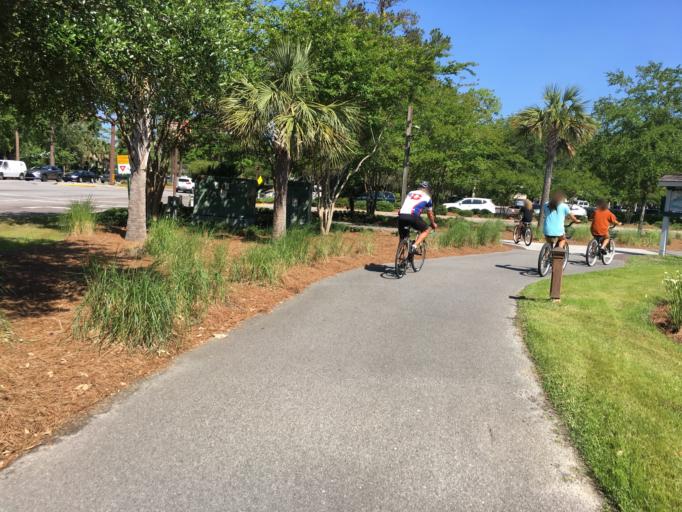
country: US
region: South Carolina
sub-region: Beaufort County
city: Hilton Head Island
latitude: 32.1533
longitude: -80.7605
